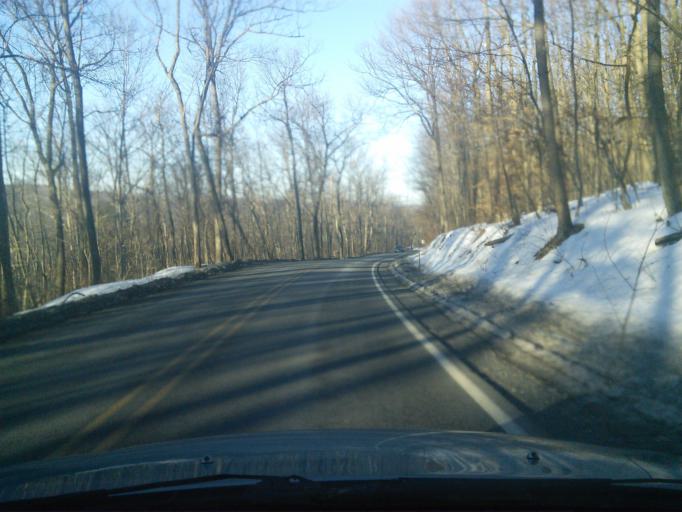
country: US
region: Pennsylvania
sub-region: Centre County
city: Park Forest Village
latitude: 40.8520
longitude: -77.9416
